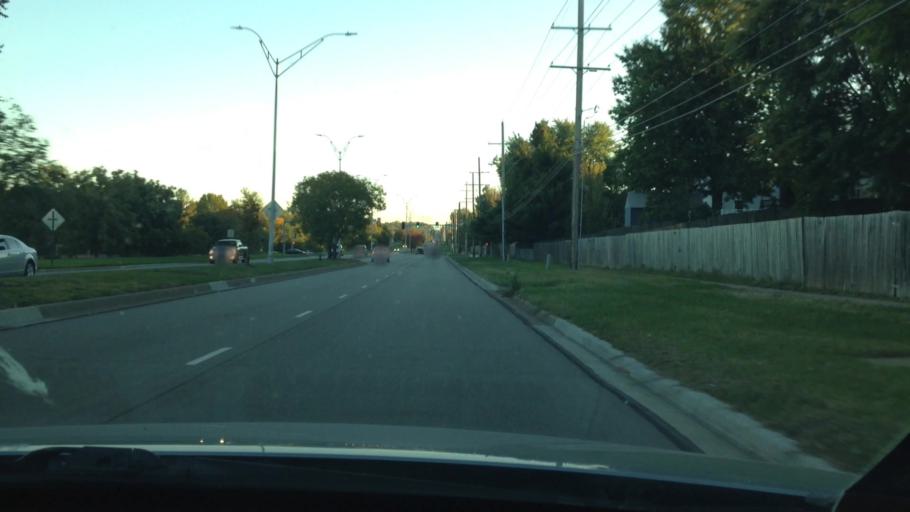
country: US
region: Kansas
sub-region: Johnson County
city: Lenexa
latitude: 38.9080
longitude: -94.7612
